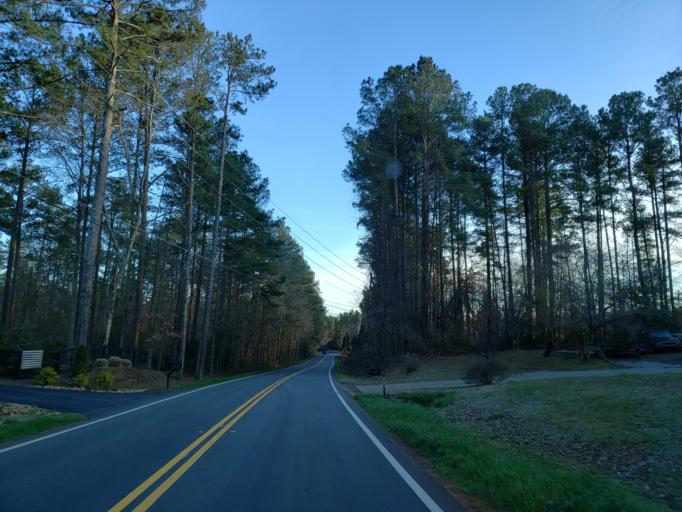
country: US
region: Georgia
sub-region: Cobb County
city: Acworth
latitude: 34.0360
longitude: -84.7282
